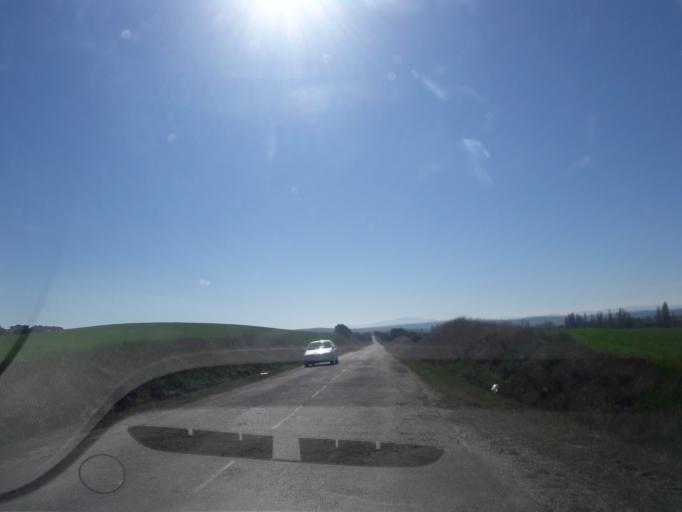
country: ES
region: Castille and Leon
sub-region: Provincia de Salamanca
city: Mancera de Abajo
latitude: 40.8220
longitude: -5.1757
